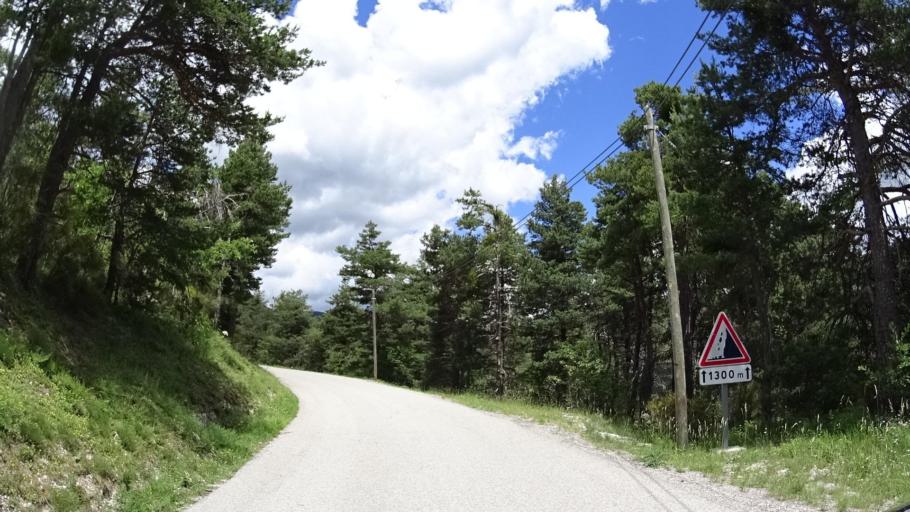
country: FR
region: Provence-Alpes-Cote d'Azur
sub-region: Departement des Alpes-de-Haute-Provence
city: Annot
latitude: 44.0159
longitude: 6.6265
